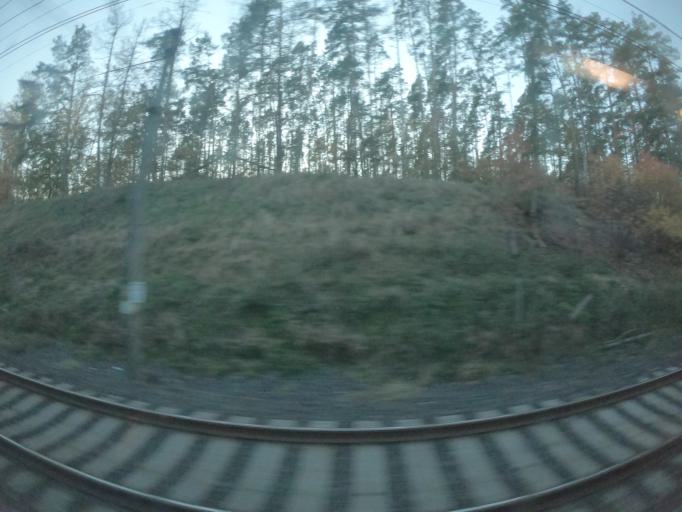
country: PL
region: West Pomeranian Voivodeship
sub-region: Powiat mysliborski
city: Boleszkowice
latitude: 52.7179
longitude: 14.5307
